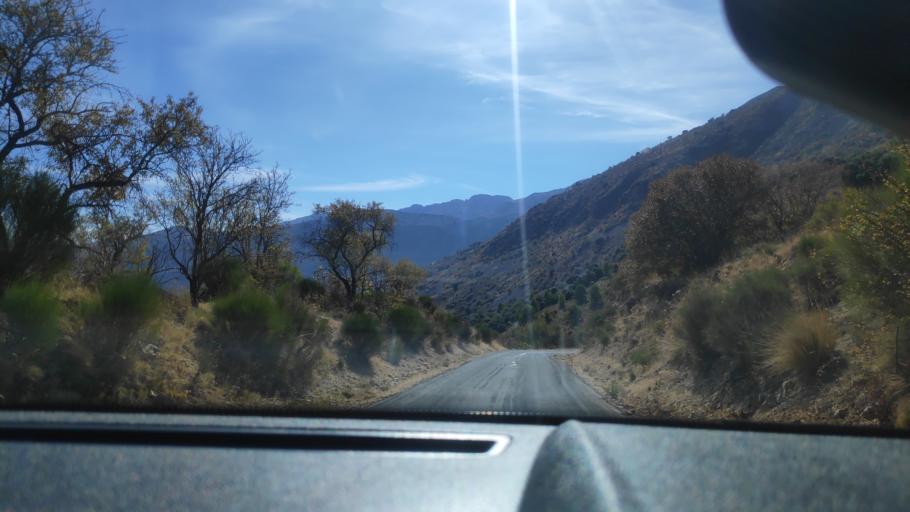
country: ES
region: Andalusia
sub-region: Provincia de Jaen
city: Torres
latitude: 37.7846
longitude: -3.4803
